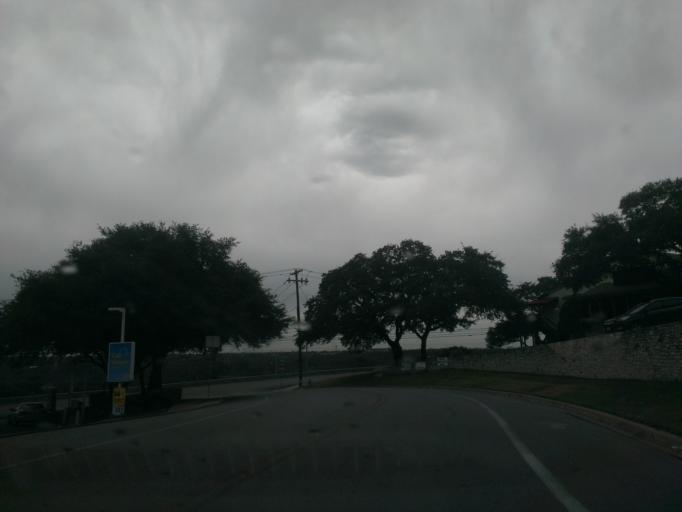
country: US
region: Texas
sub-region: Travis County
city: West Lake Hills
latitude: 30.3571
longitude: -97.7475
